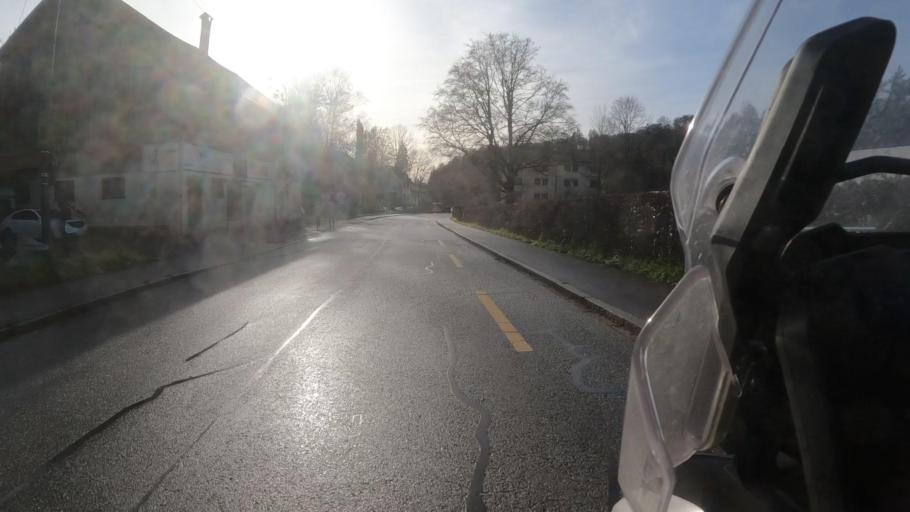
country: CH
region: Schaffhausen
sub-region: Bezirk Schaffhausen
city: Neuhausen
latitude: 47.6993
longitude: 8.6203
